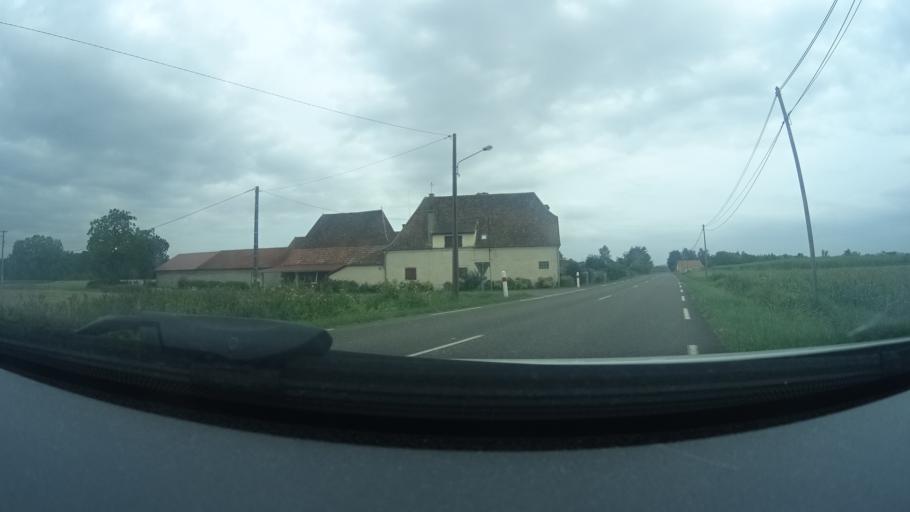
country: FR
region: Aquitaine
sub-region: Departement des Pyrenees-Atlantiques
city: Mont
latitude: 43.4529
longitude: -0.7057
